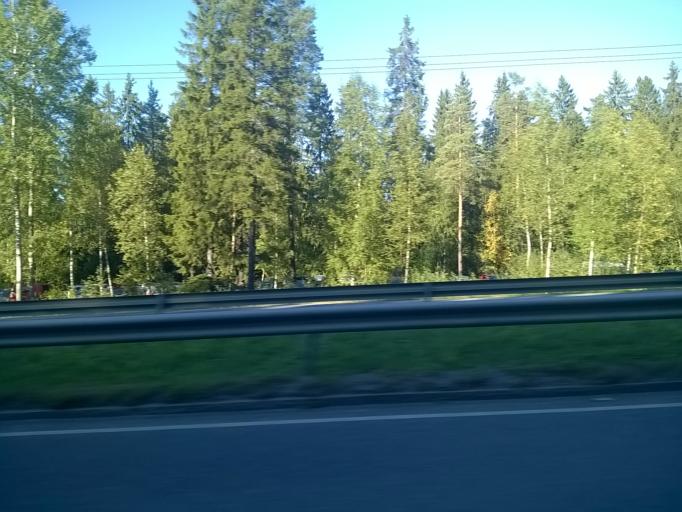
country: FI
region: Pirkanmaa
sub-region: Tampere
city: Tampere
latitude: 61.5019
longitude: 23.8672
